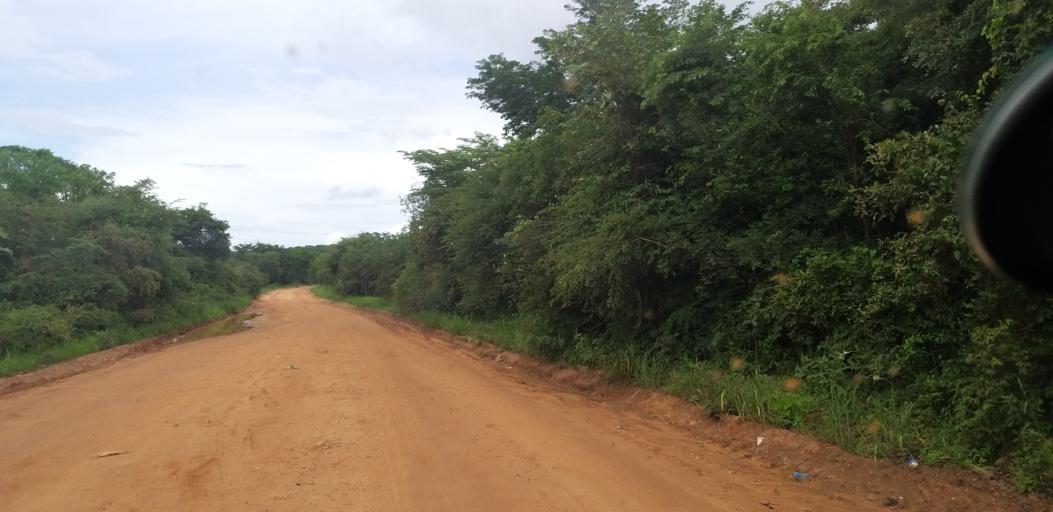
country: ZM
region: Lusaka
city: Lusaka
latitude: -15.1911
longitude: 28.4450
